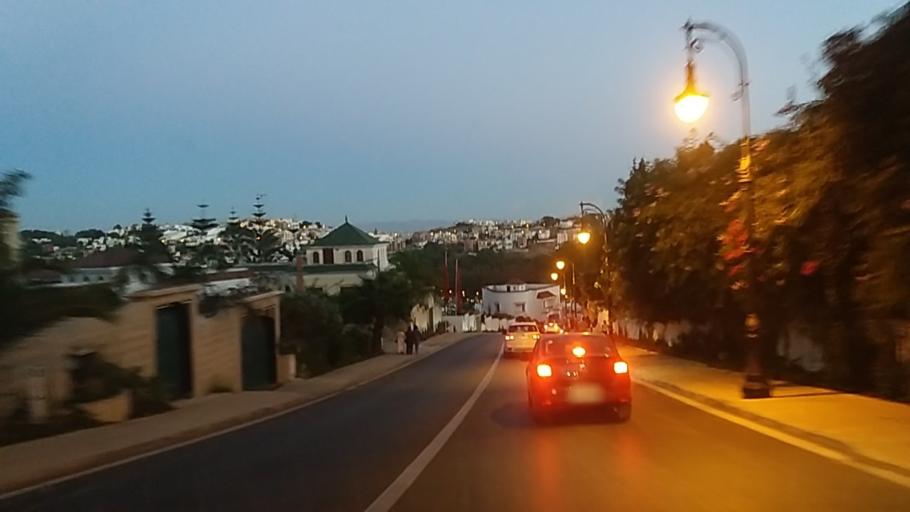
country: MA
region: Tanger-Tetouan
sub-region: Tanger-Assilah
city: Tangier
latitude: 35.7851
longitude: -5.8435
